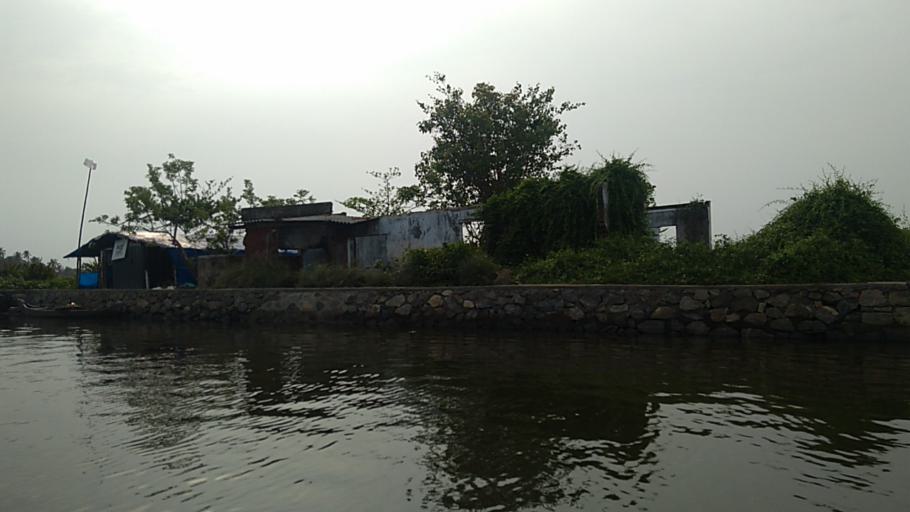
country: IN
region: Kerala
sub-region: Ernakulam
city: Elur
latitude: 10.0570
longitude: 76.2529
